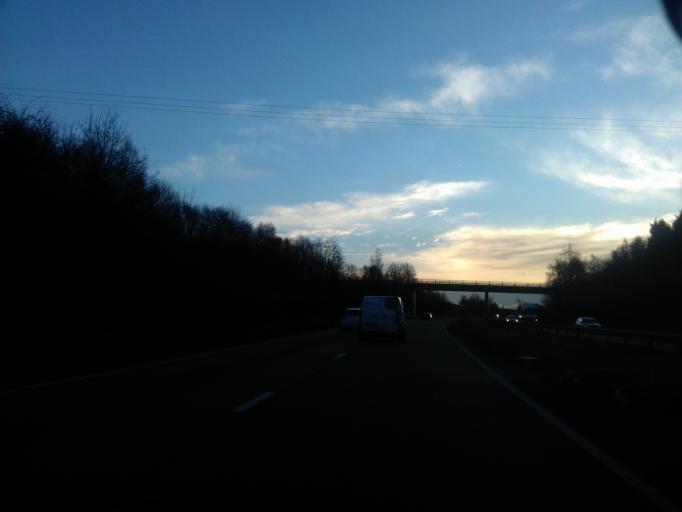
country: GB
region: England
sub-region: Essex
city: Wivenhoe
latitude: 51.9084
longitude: 0.9637
